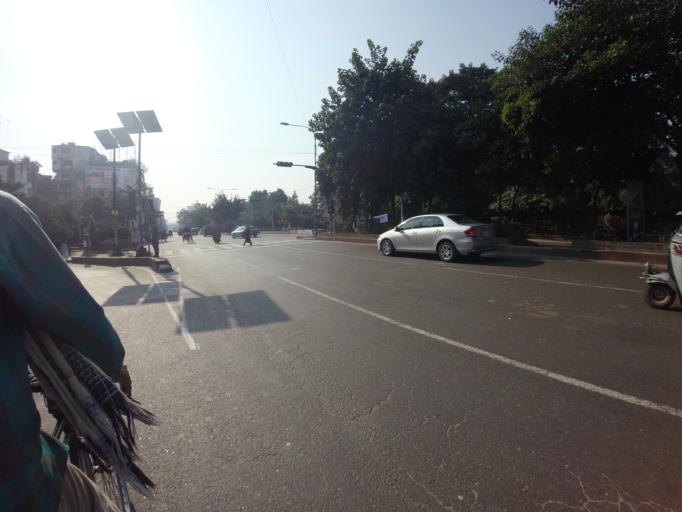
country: BD
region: Dhaka
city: Azimpur
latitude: 23.7516
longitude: 90.3782
